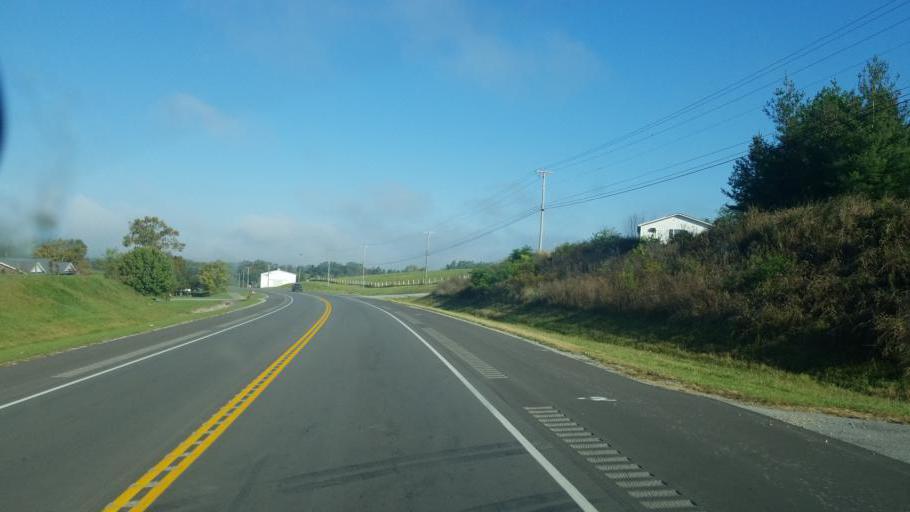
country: US
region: Kentucky
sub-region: Fleming County
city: Flemingsburg
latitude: 38.4576
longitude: -83.7497
